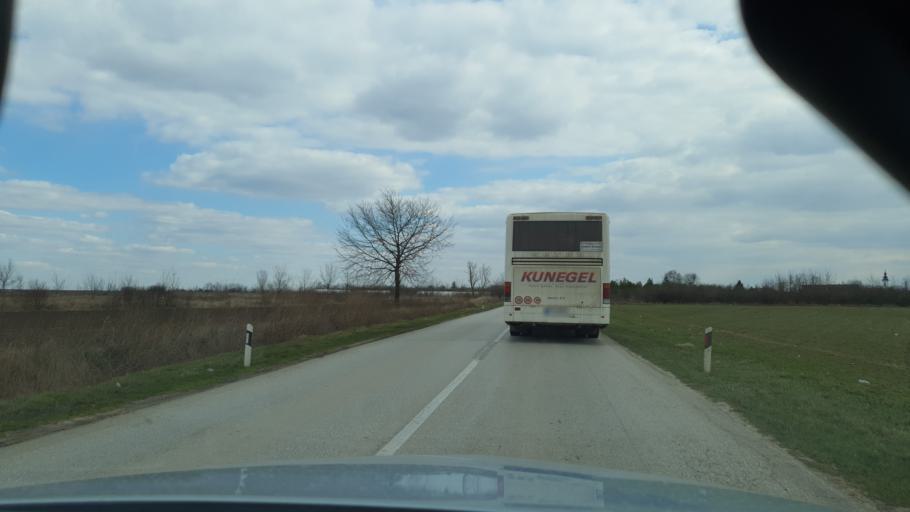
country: RS
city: Obrovac
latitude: 45.4206
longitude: 19.3984
